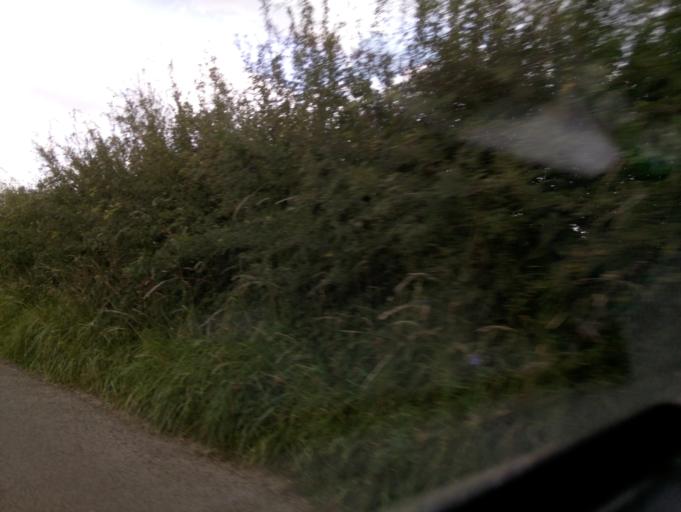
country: GB
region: England
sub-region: Gloucestershire
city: Chalford
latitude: 51.7670
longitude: -2.0905
